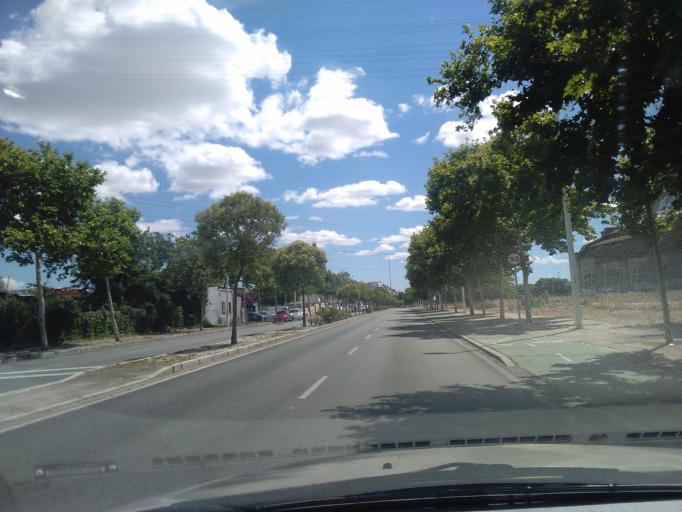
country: ES
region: Andalusia
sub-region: Provincia de Sevilla
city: Sevilla
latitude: 37.4178
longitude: -5.9856
